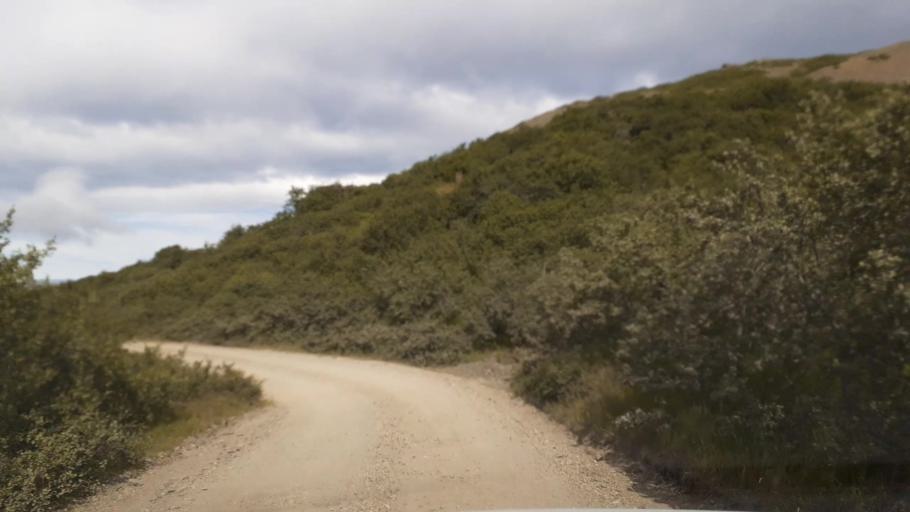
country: IS
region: East
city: Hoefn
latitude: 64.4392
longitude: -14.9155
